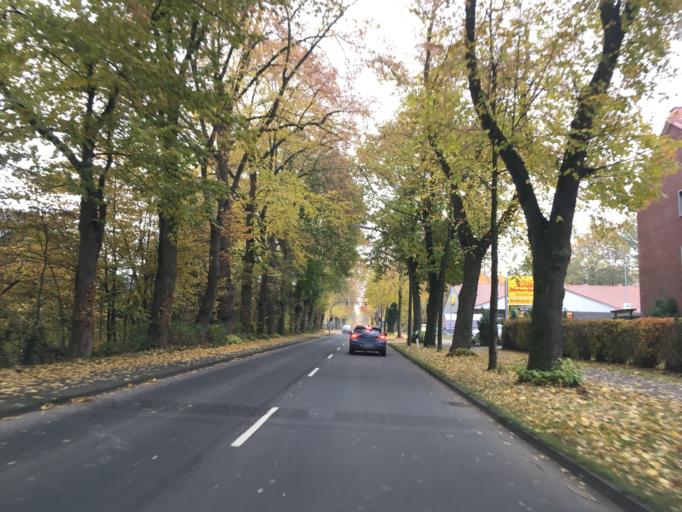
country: DE
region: North Rhine-Westphalia
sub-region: Regierungsbezirk Munster
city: Telgte
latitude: 51.9866
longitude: 7.7942
